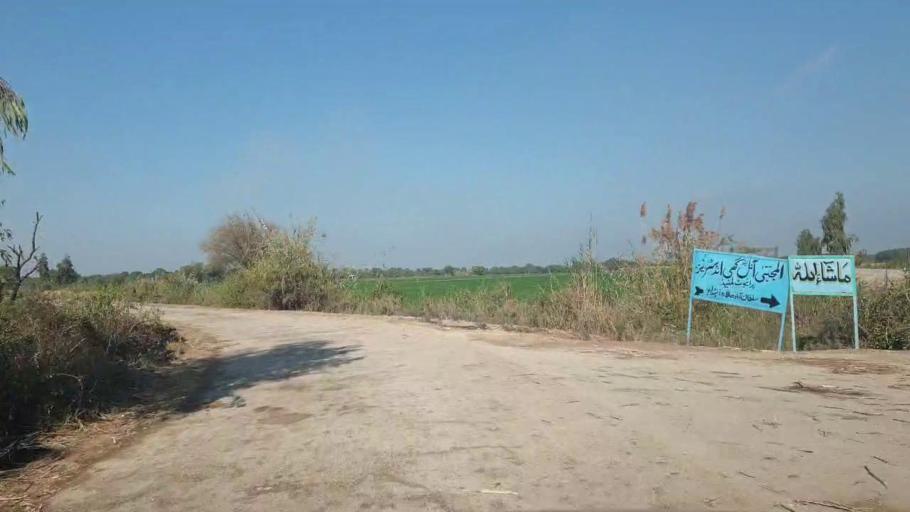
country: PK
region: Sindh
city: Shahdadpur
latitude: 25.9112
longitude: 68.5954
